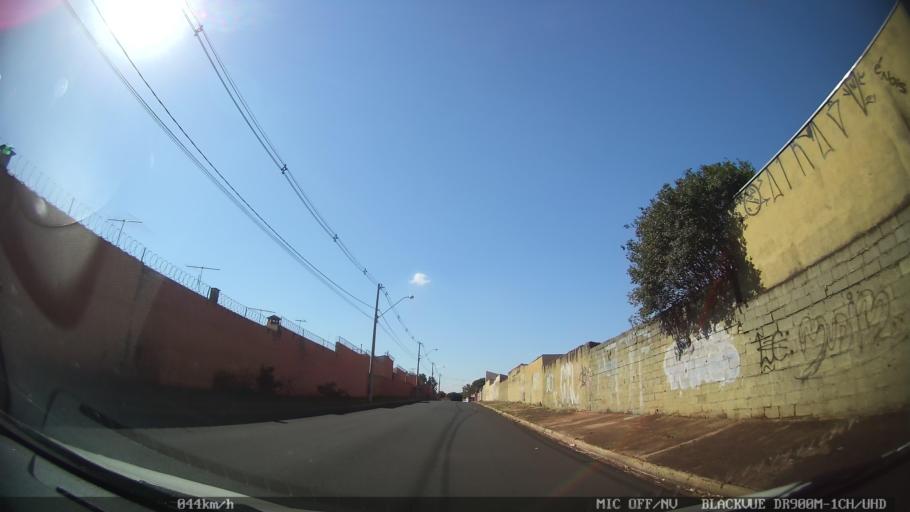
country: BR
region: Sao Paulo
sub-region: Ribeirao Preto
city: Ribeirao Preto
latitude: -21.2200
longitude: -47.7665
